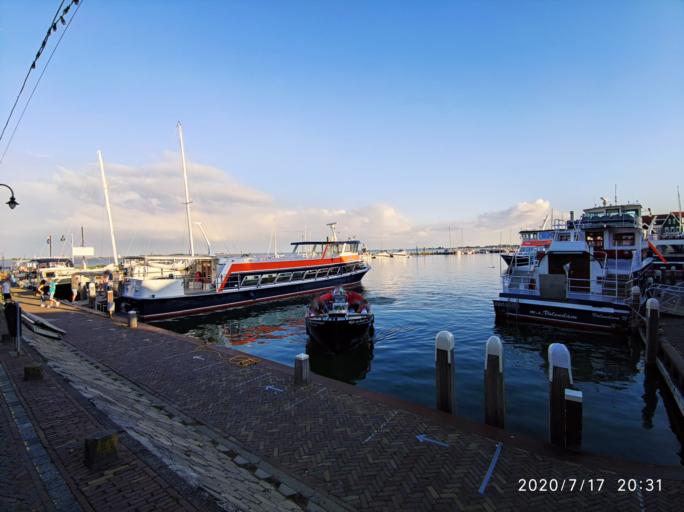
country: NL
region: North Holland
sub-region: Gemeente Edam-Volendam
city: Volendam
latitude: 52.4944
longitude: 5.0770
